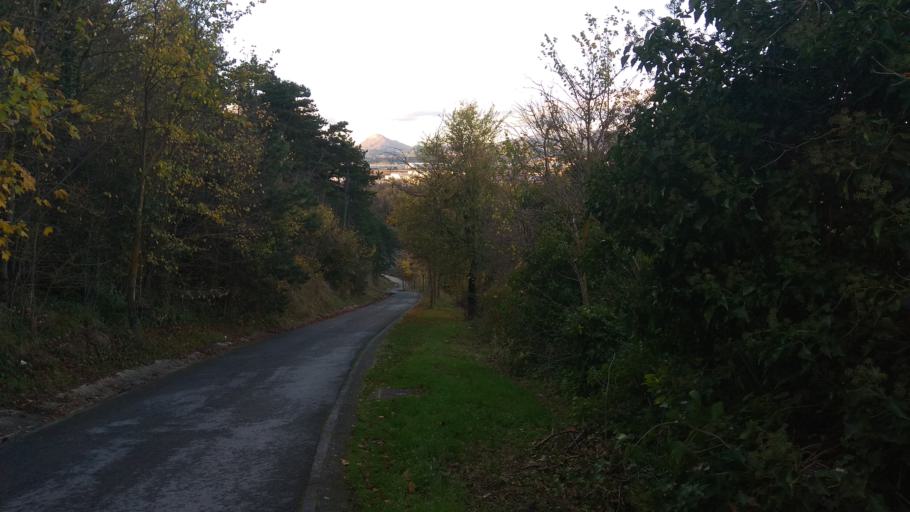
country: ES
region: Navarre
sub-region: Provincia de Navarra
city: Cizur Mayor
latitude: 42.7945
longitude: -1.6952
